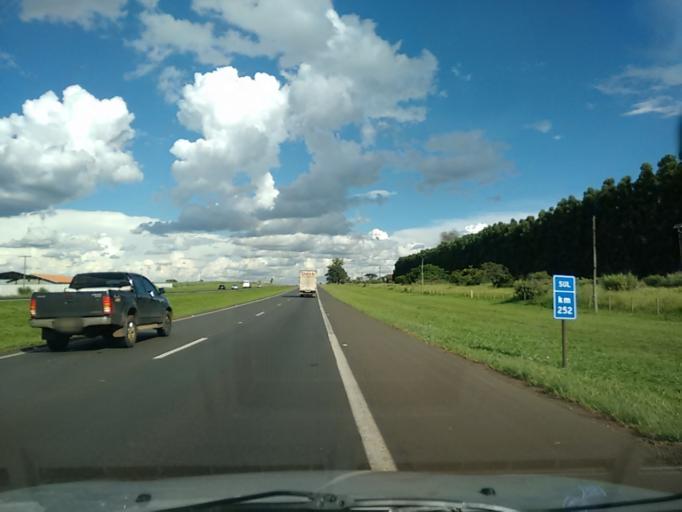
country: BR
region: Sao Paulo
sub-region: Ibate
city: Ibate
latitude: -21.9246
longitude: -48.0290
